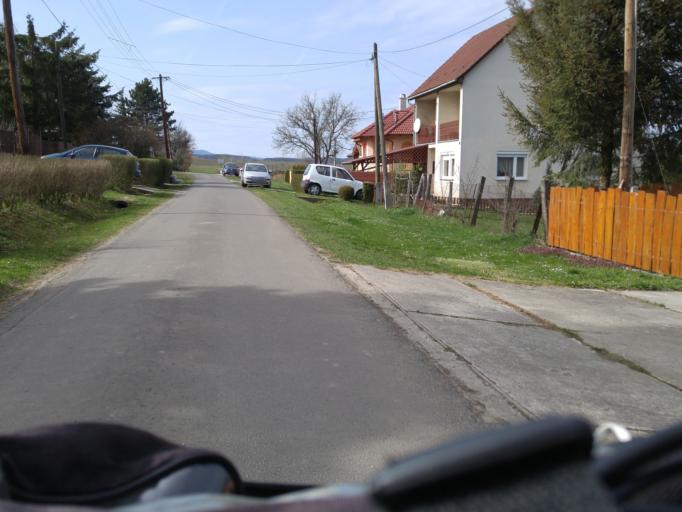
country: HU
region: Nograd
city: Retsag
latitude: 47.9250
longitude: 19.1686
